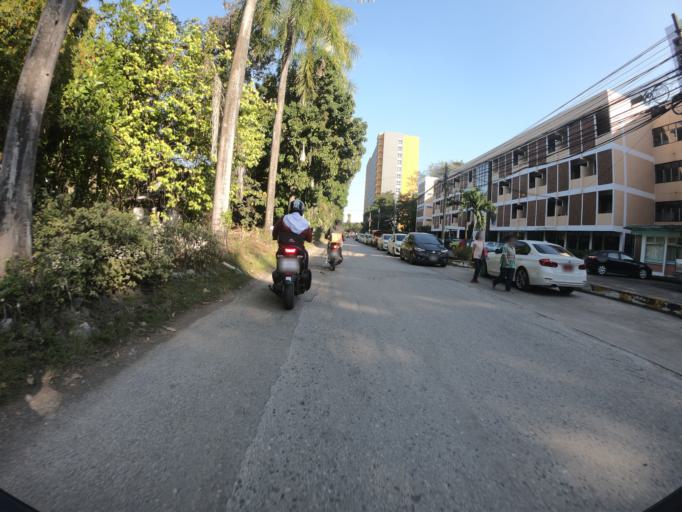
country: TH
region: Chiang Mai
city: Chiang Mai
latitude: 18.7932
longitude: 98.9684
